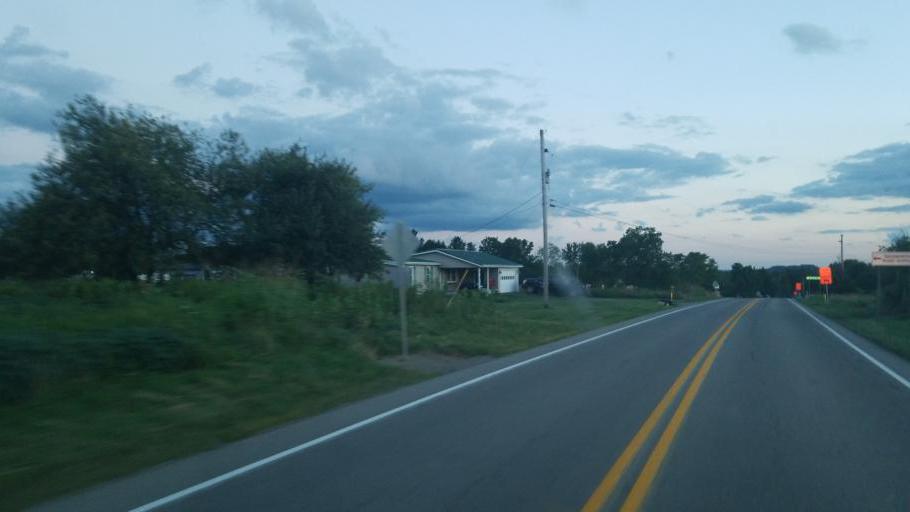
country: US
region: Pennsylvania
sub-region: Clarion County
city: Knox
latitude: 41.1948
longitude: -79.5461
